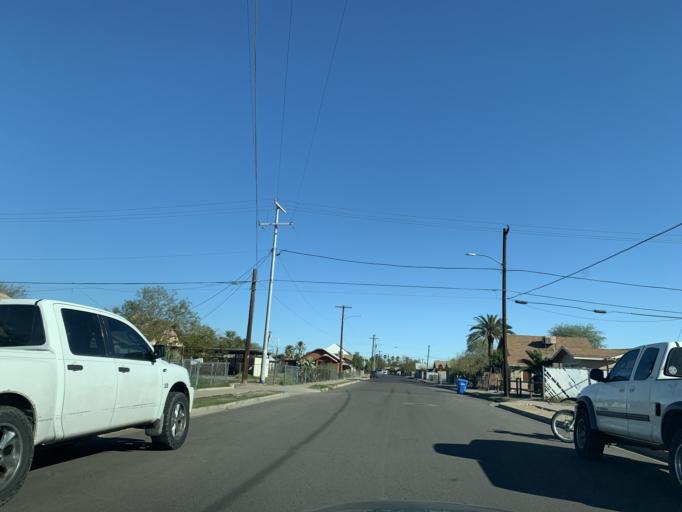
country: US
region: Arizona
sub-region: Maricopa County
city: Phoenix
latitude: 33.4529
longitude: -112.0569
